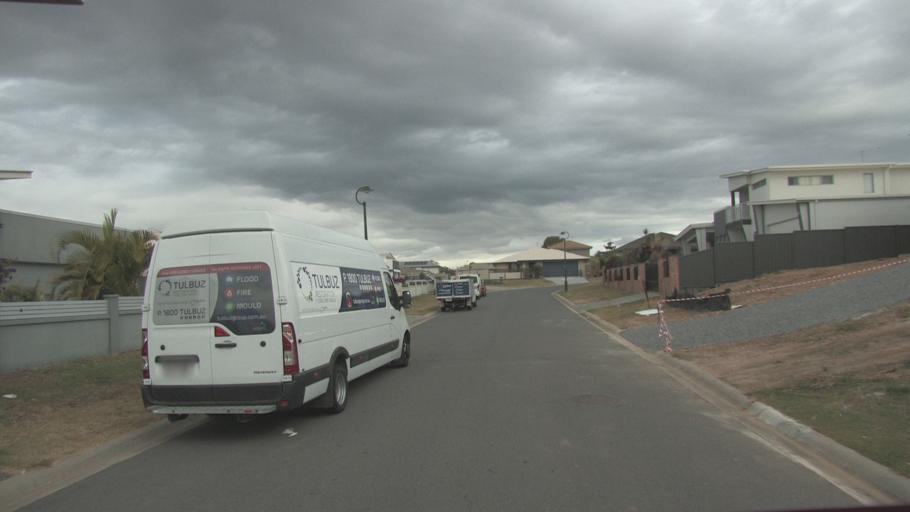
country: AU
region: Queensland
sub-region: Logan
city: Park Ridge South
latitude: -27.6838
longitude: 153.0456
